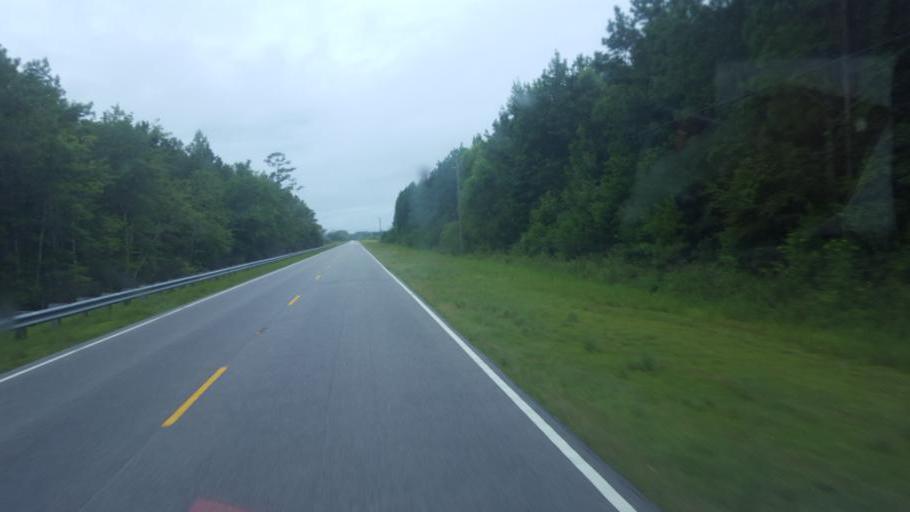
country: US
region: North Carolina
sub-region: Tyrrell County
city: Columbia
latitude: 35.9030
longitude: -76.0890
